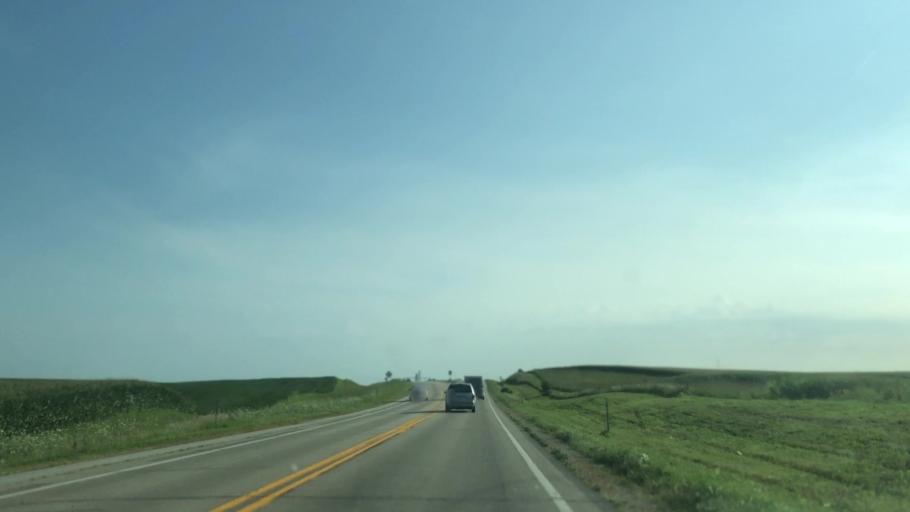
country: US
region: Iowa
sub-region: Marshall County
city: Marshalltown
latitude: 42.0184
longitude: -93.0124
